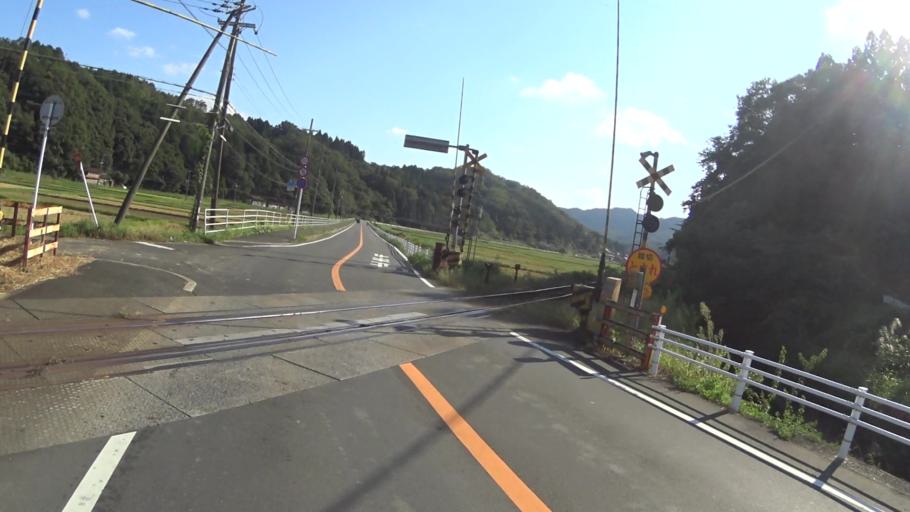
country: JP
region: Kyoto
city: Miyazu
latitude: 35.6661
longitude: 135.0236
